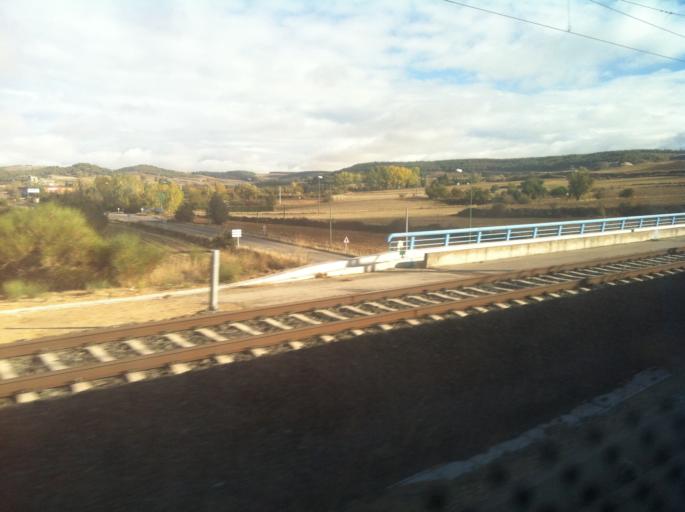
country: ES
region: Castille and Leon
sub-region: Provincia de Burgos
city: Burgos
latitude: 42.3675
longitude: -3.6931
